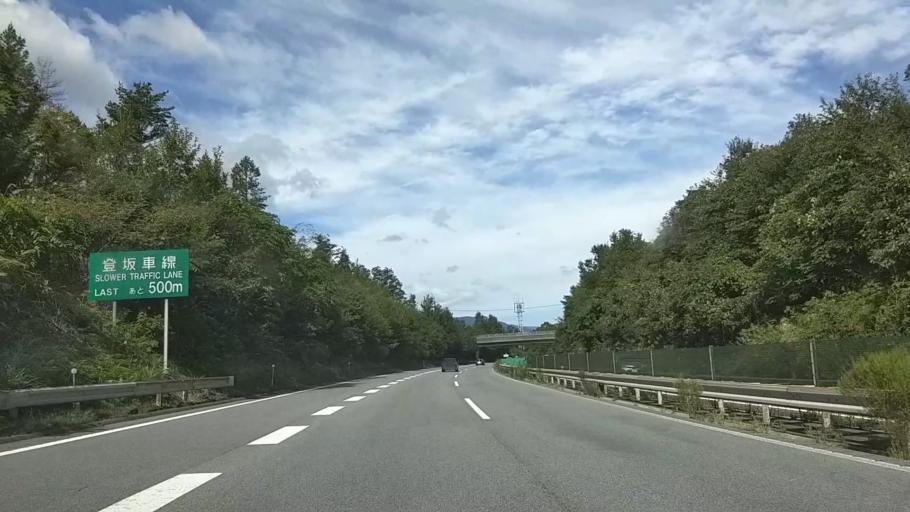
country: JP
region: Yamanashi
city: Nirasaki
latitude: 35.7924
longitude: 138.4021
